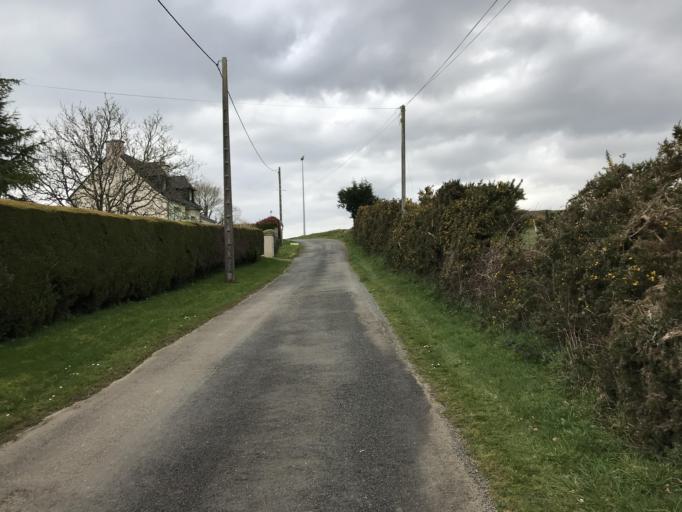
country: FR
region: Brittany
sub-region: Departement du Finistere
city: Hopital-Camfrout
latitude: 48.3222
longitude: -4.2290
